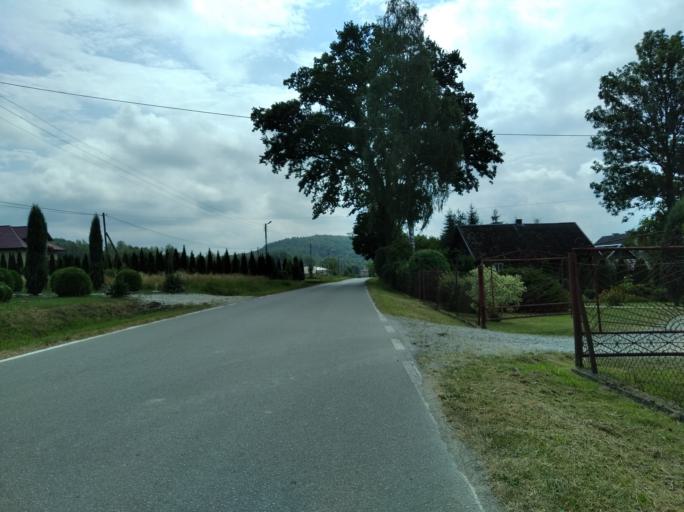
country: PL
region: Subcarpathian Voivodeship
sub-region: Powiat krosnienski
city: Wojaszowka
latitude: 49.7921
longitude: 21.6886
